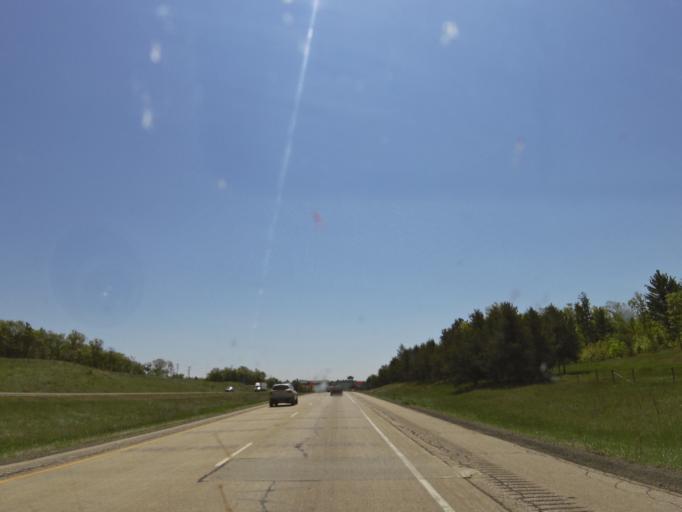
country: US
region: Wisconsin
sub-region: Monroe County
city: Tomah
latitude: 44.1371
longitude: -90.5386
